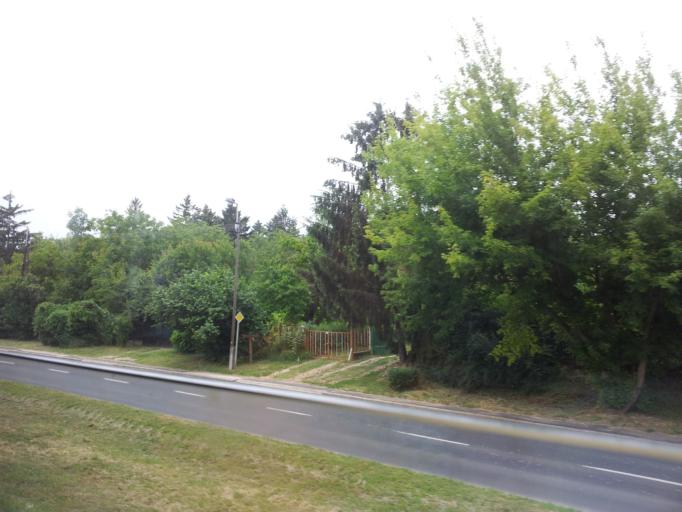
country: HU
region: Veszprem
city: Revfueloep
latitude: 46.8202
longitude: 17.5750
